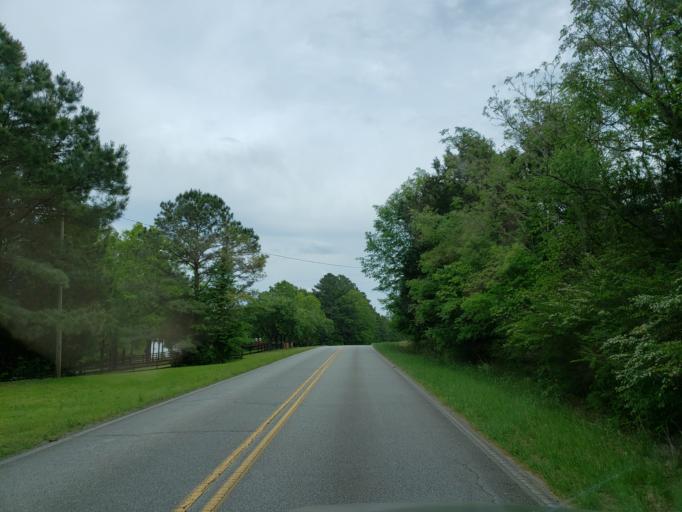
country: US
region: Georgia
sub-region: Bibb County
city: West Point
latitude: 32.8305
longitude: -83.8876
